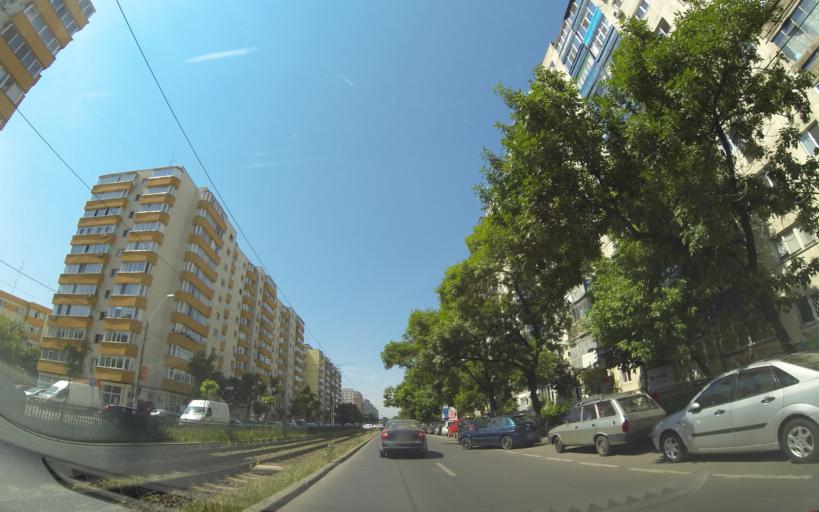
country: RO
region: Bucuresti
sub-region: Municipiul Bucuresti
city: Bucuresti
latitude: 44.4117
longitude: 26.0714
